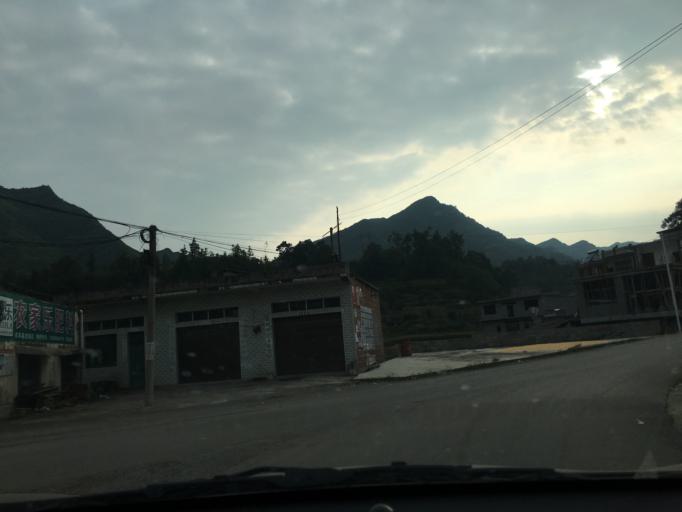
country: CN
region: Guangxi Zhuangzu Zizhiqu
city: Xinzhou
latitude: 25.4357
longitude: 105.4780
